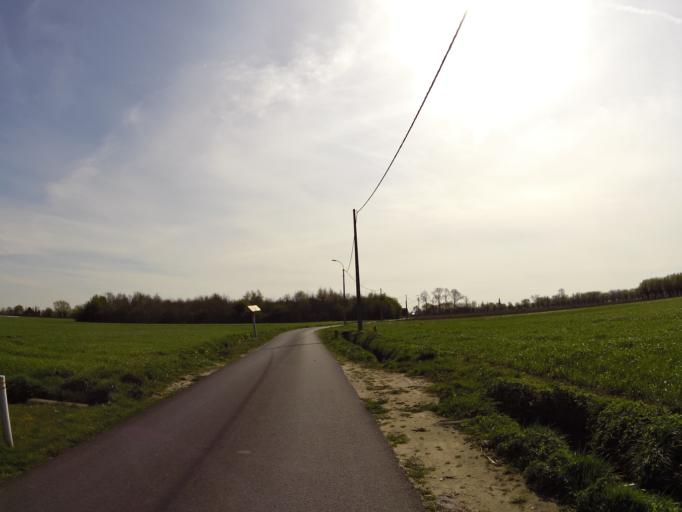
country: BE
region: Flanders
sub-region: Provincie West-Vlaanderen
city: Jabbeke
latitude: 51.1490
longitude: 3.0440
